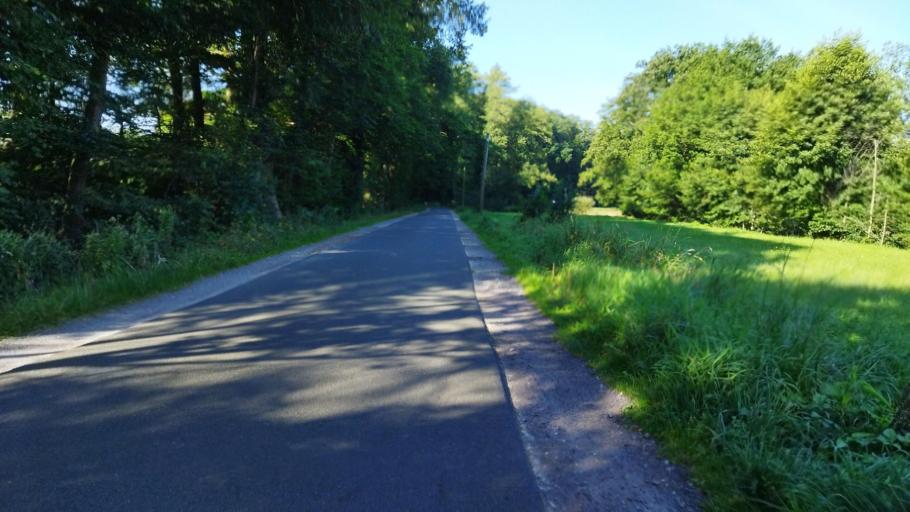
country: DE
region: North Rhine-Westphalia
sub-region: Regierungsbezirk Munster
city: Lienen
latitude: 52.1357
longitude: 7.9971
